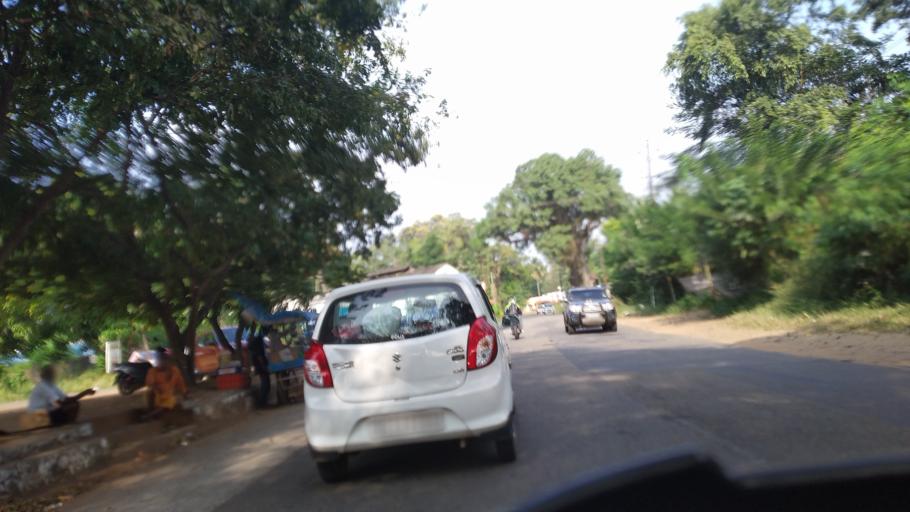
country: IN
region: Kerala
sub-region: Thrissur District
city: Chelakara
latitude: 10.5932
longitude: 76.5212
